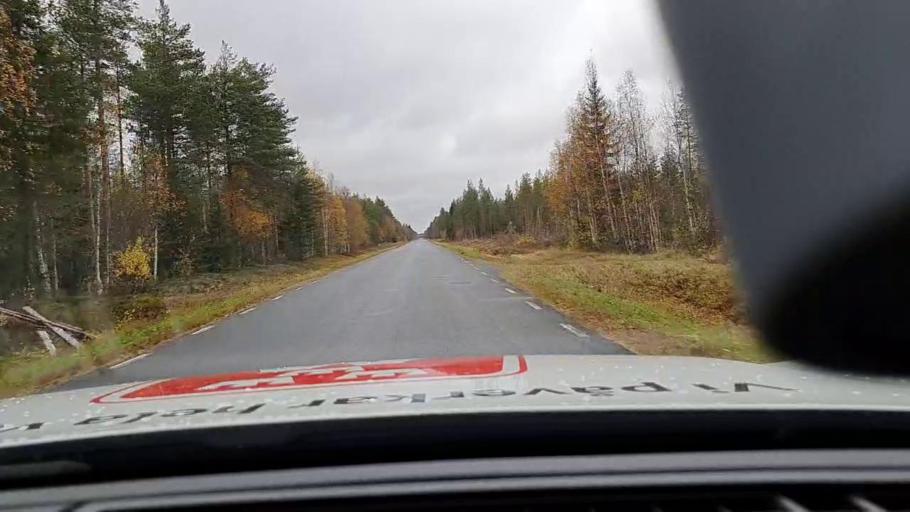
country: SE
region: Norrbotten
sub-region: Haparanda Kommun
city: Haparanda
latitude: 65.9084
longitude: 23.8310
